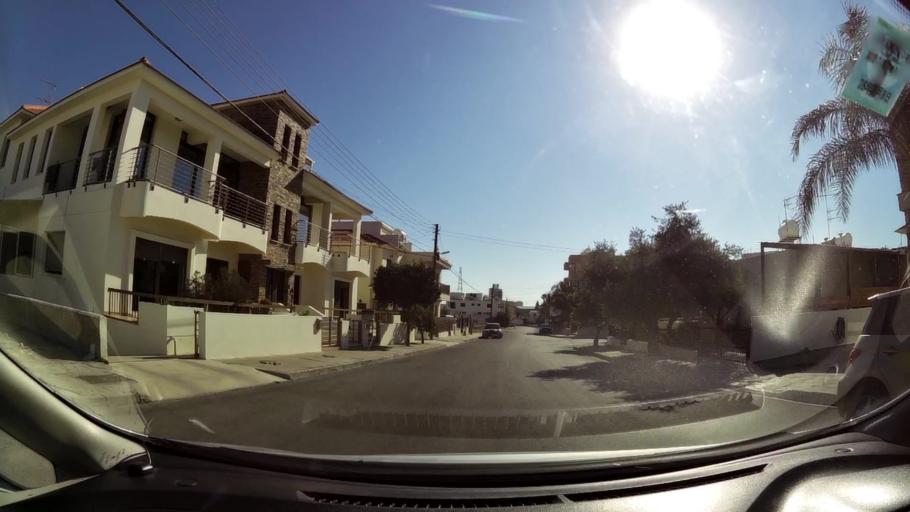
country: CY
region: Larnaka
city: Larnaca
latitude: 34.9320
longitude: 33.6191
